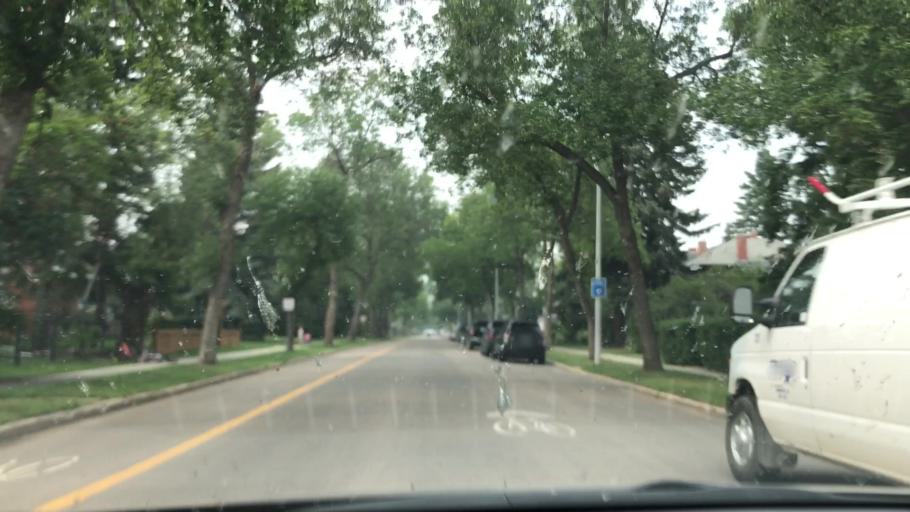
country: CA
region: Alberta
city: Edmonton
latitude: 53.5605
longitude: -113.5412
